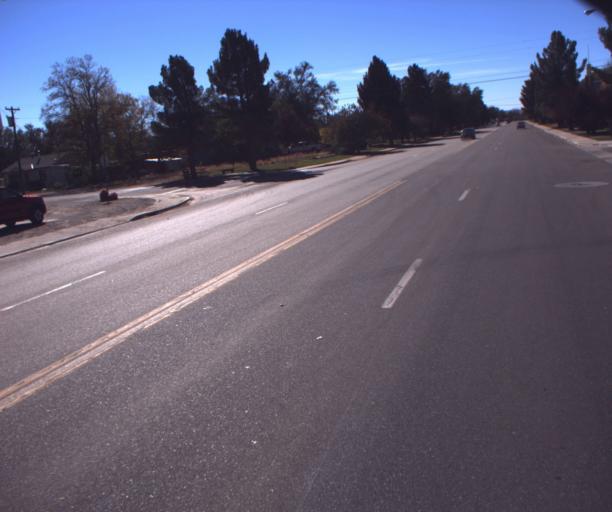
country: US
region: Arizona
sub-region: Coconino County
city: Fredonia
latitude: 36.9495
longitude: -112.5265
